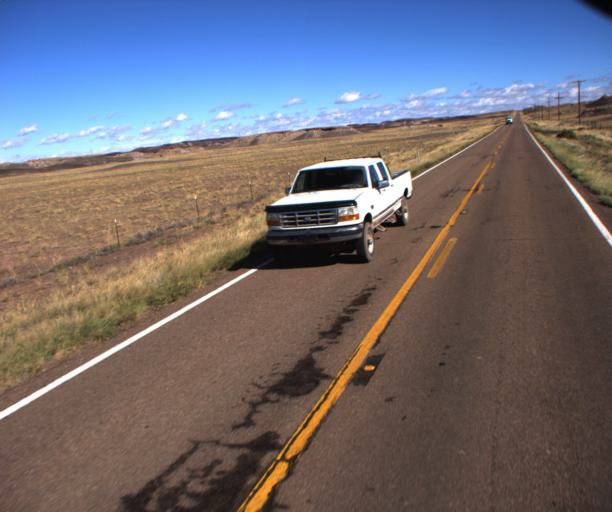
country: US
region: Arizona
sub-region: Apache County
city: Saint Johns
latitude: 34.5437
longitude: -109.3441
